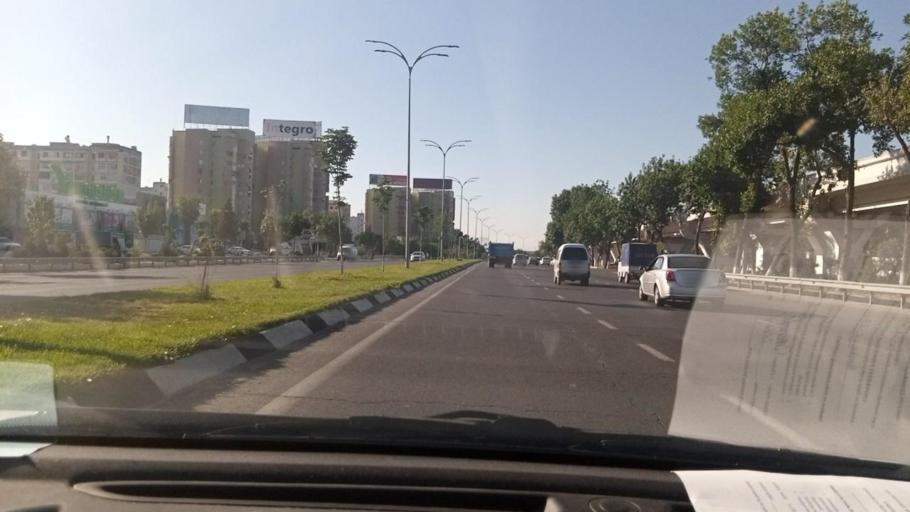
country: UZ
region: Toshkent
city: Salor
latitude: 41.2917
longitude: 69.3570
